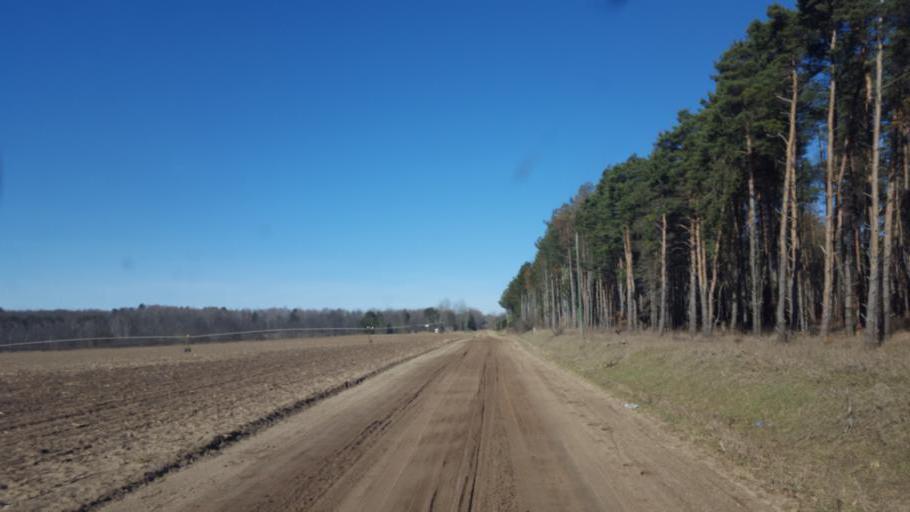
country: US
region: Michigan
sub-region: Isabella County
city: Lake Isabella
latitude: 43.5383
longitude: -85.0120
